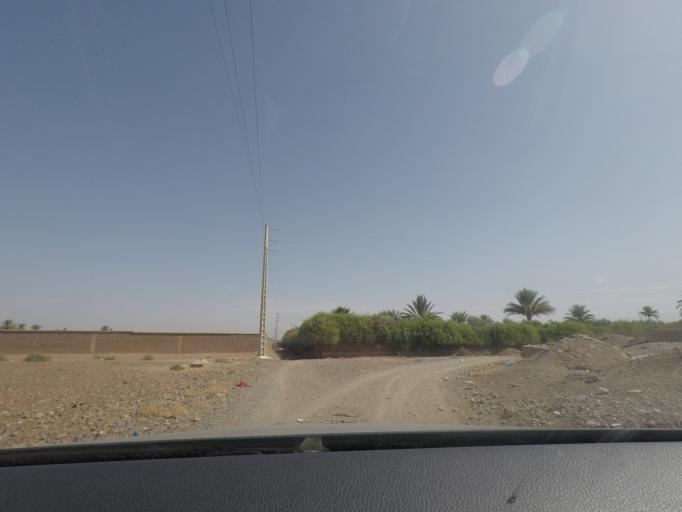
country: MA
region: Marrakech-Tensift-Al Haouz
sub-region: Marrakech
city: Marrakesh
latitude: 31.5792
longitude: -8.0255
